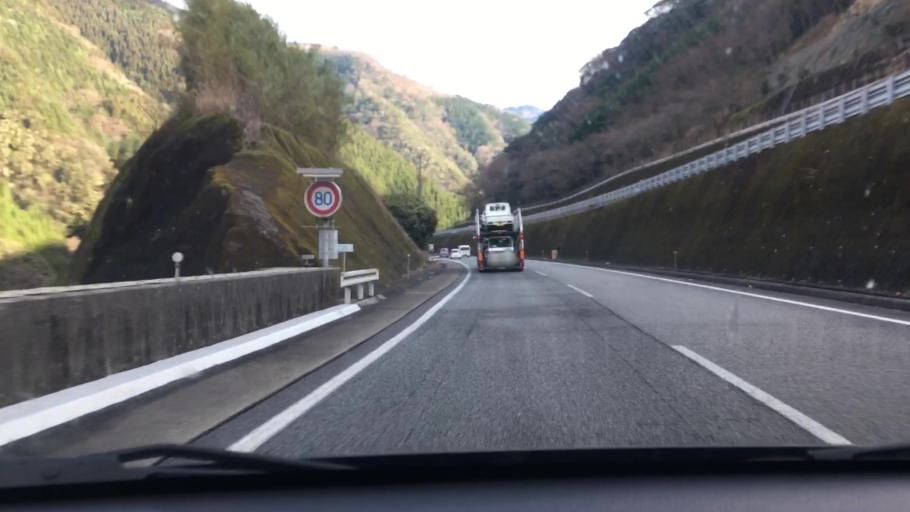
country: JP
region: Kumamoto
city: Hitoyoshi
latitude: 32.3280
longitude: 130.7510
